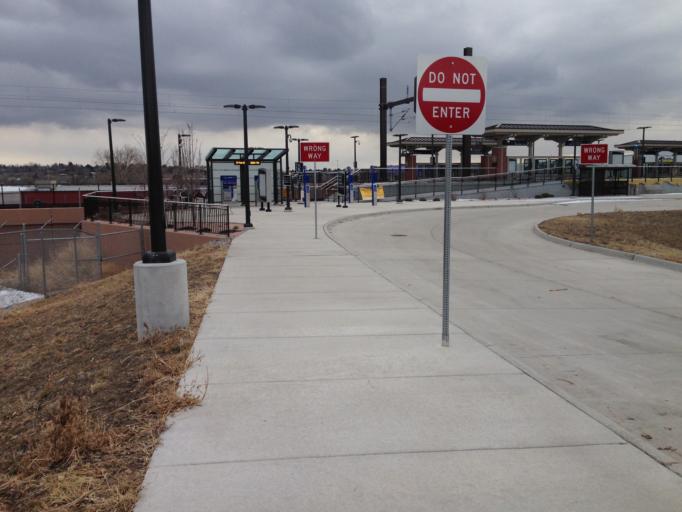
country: US
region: Colorado
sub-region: Adams County
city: Berkley
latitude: 39.8042
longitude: -105.0487
